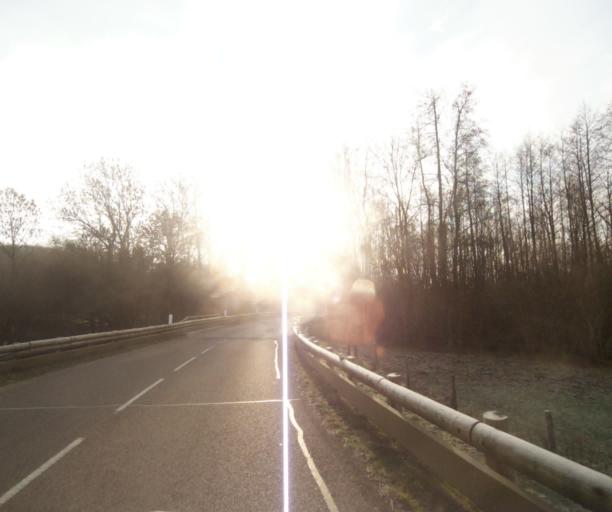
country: FR
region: Champagne-Ardenne
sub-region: Departement de la Marne
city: Sermaize-les-Bains
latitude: 48.7458
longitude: 4.9060
